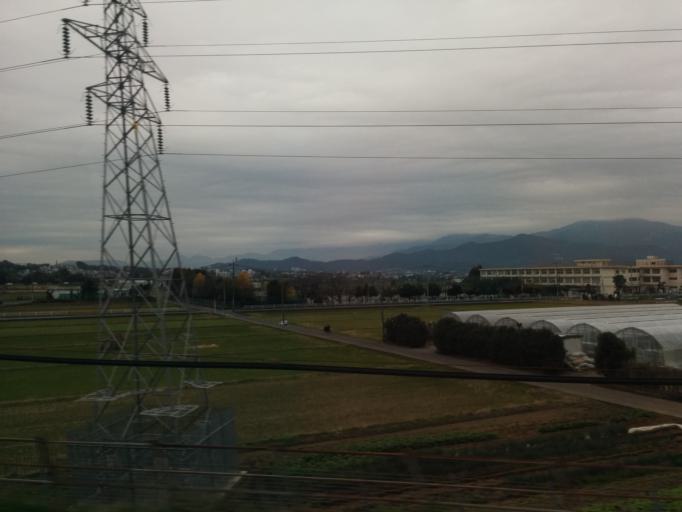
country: JP
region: Kanagawa
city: Hiratsuka
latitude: 35.3525
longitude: 139.3172
